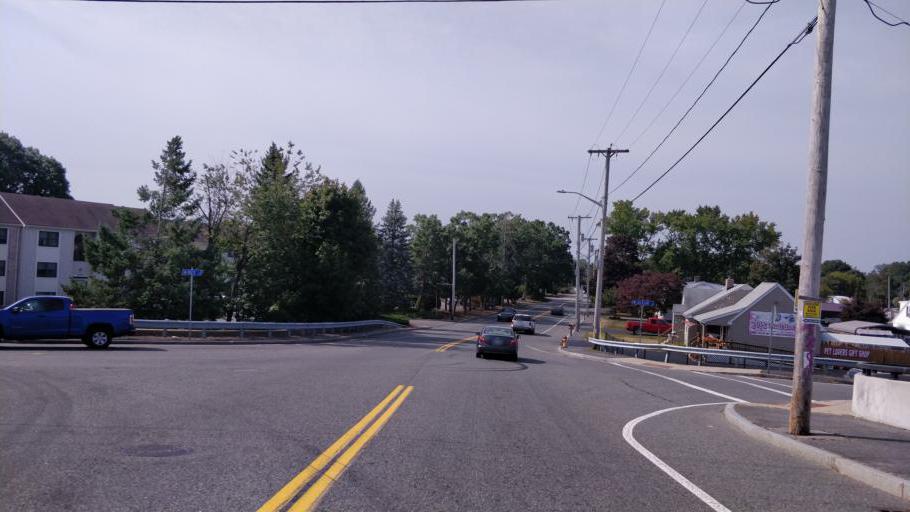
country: US
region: Massachusetts
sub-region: Bristol County
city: North Seekonk
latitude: 41.8989
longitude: -71.3464
